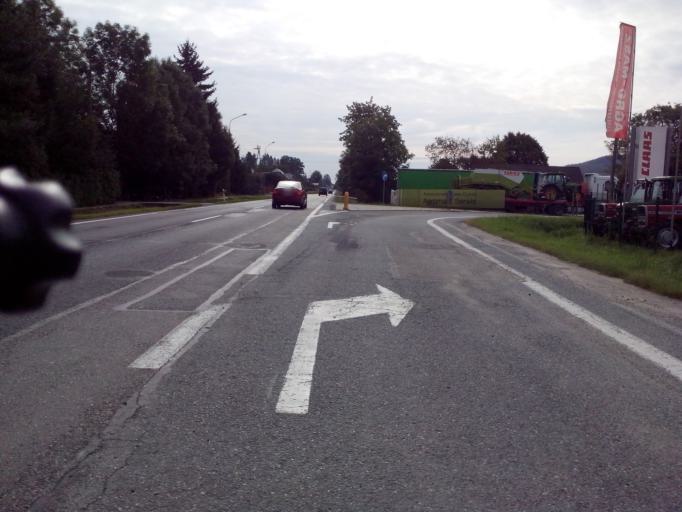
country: PL
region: Subcarpathian Voivodeship
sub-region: Powiat brzozowski
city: Domaradz
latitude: 49.7962
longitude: 21.9411
